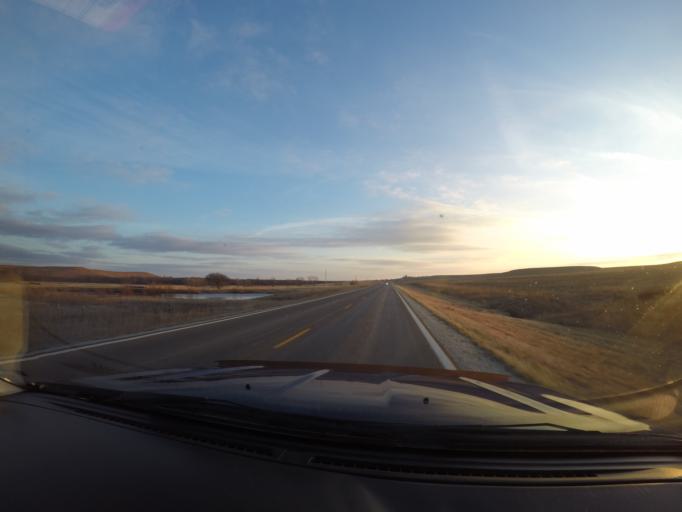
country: US
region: Kansas
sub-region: Chase County
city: Cottonwood Falls
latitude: 38.4226
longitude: -96.5571
